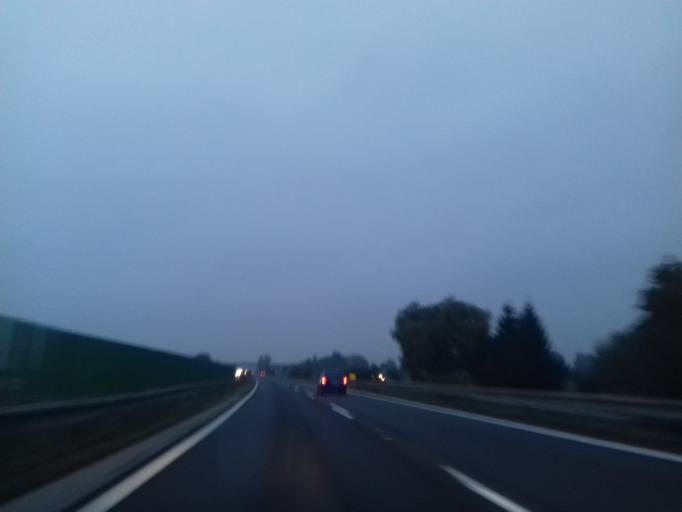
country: CZ
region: Olomoucky
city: Naklo
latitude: 49.6454
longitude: 17.1329
